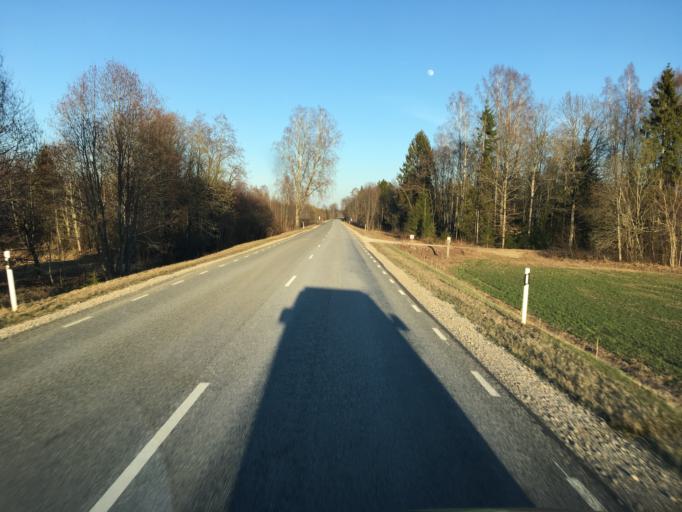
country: EE
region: Raplamaa
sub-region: Rapla vald
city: Rapla
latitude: 59.0757
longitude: 24.8742
